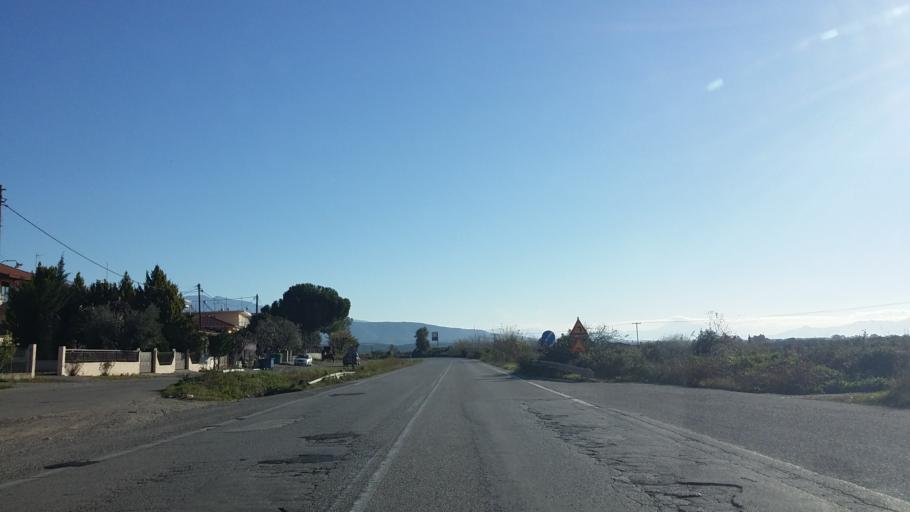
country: GR
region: West Greece
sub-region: Nomos Aitolias kai Akarnanias
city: Lepenou
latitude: 38.6663
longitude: 21.3081
